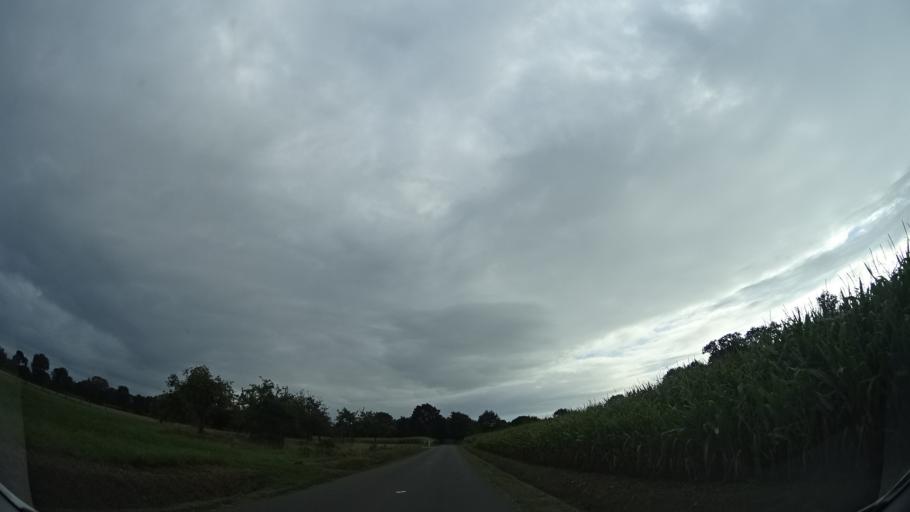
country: FR
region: Brittany
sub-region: Departement d'Ille-et-Vilaine
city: Hede-Bazouges
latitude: 48.3045
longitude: -1.7852
